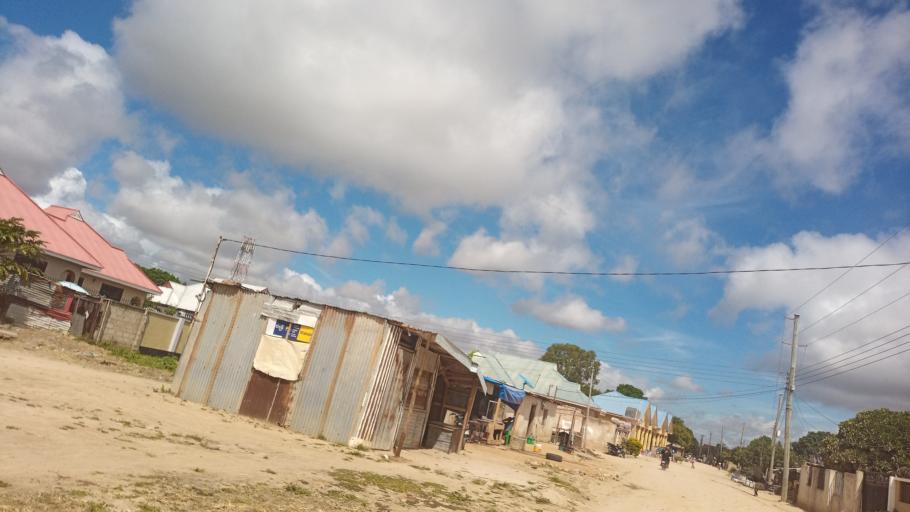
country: TZ
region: Dodoma
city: Kisasa
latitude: -6.1755
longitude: 35.7706
